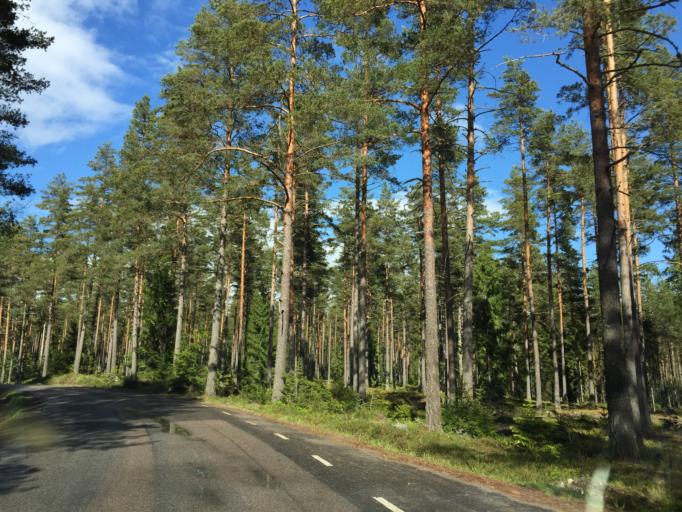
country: SE
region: Soedermanland
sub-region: Vingakers Kommun
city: Vingaker
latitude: 58.9705
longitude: 15.6773
